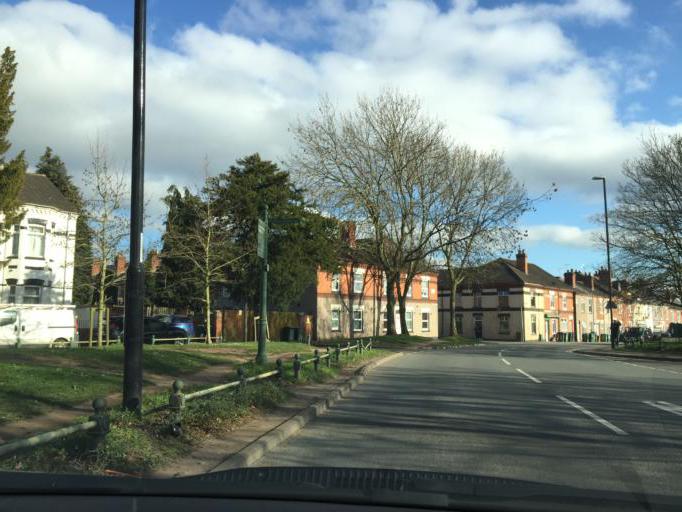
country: GB
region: England
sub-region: Coventry
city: Coventry
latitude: 52.4122
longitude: -1.4933
